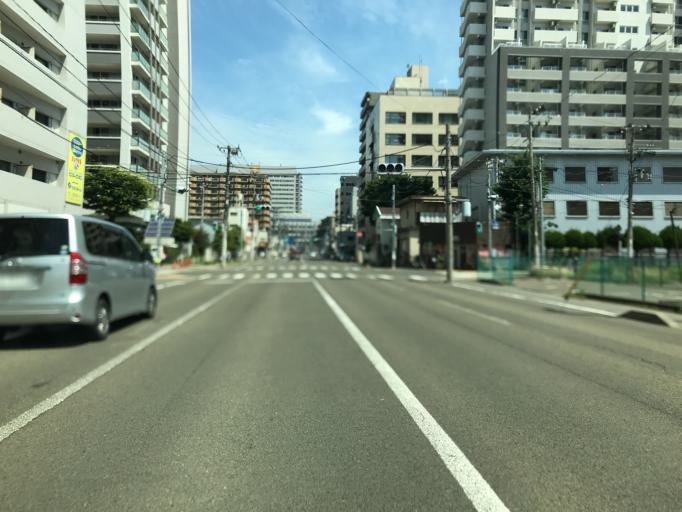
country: JP
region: Miyagi
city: Sendai-shi
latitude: 38.2681
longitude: 140.8625
